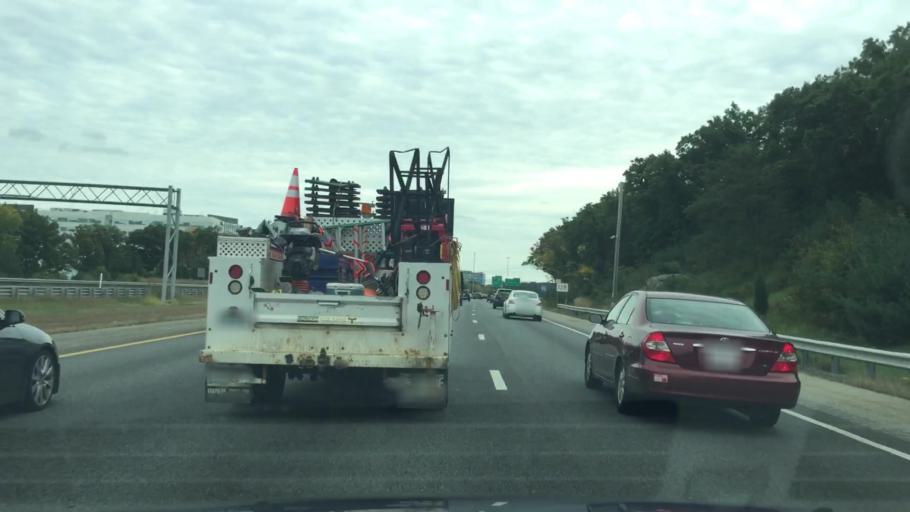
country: US
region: Massachusetts
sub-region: Middlesex County
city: Burlington
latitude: 42.4854
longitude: -71.2269
